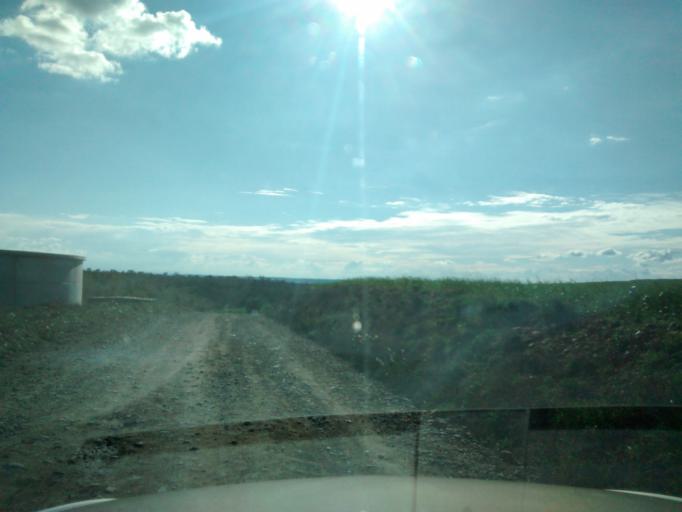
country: ES
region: Aragon
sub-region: Provincia de Zaragoza
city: San Mateo de Gallego
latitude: 41.8345
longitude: -0.7527
